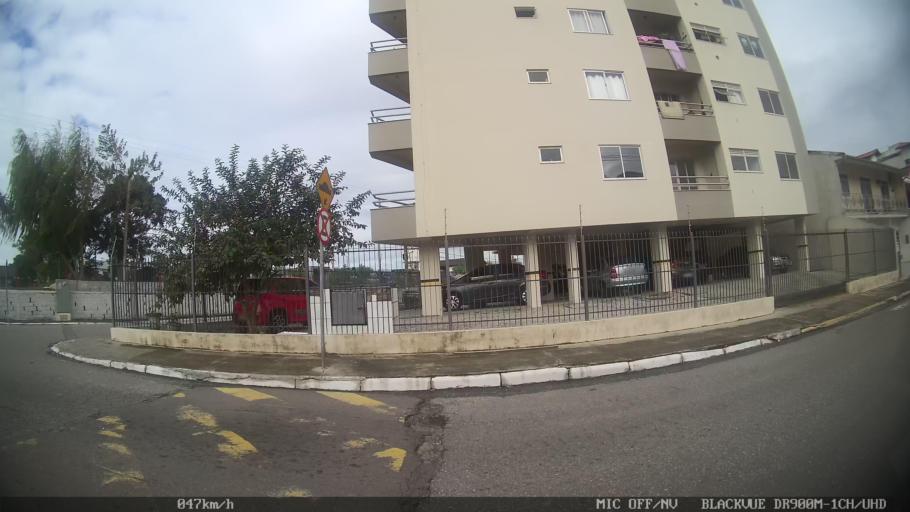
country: BR
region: Santa Catarina
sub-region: Sao Jose
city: Campinas
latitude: -27.5490
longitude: -48.6226
